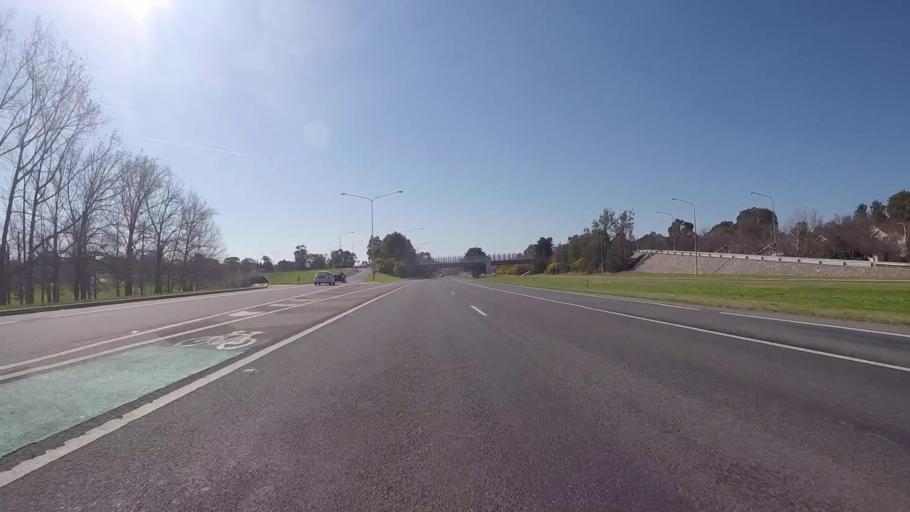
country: AU
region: Australian Capital Territory
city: Forrest
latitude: -35.3282
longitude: 149.0864
